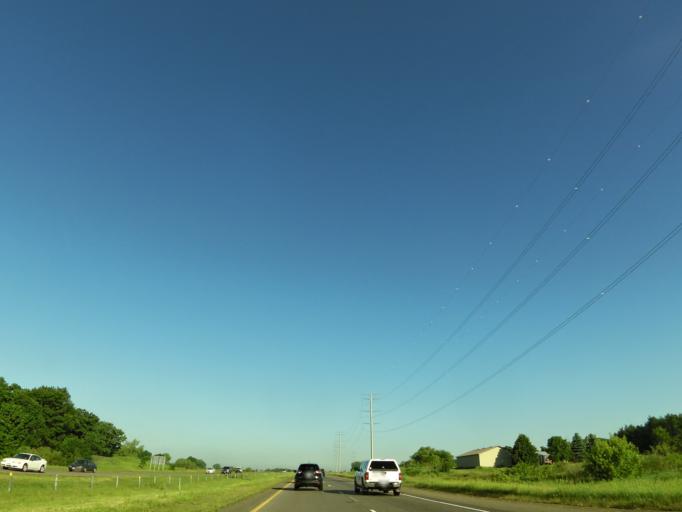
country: US
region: Minnesota
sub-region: Sherburne County
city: Becker
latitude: 45.3538
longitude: -93.9199
